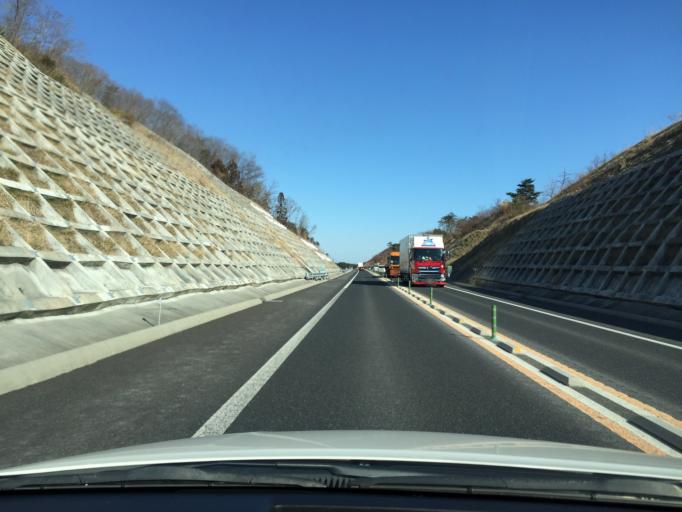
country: JP
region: Fukushima
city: Namie
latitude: 37.6916
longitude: 140.9201
